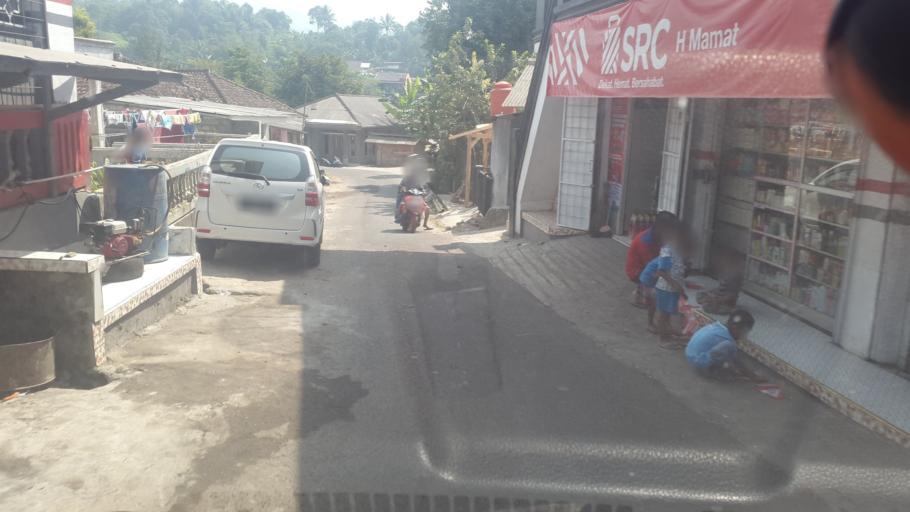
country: ID
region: West Java
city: Cicurug
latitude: -6.7697
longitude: 106.7592
